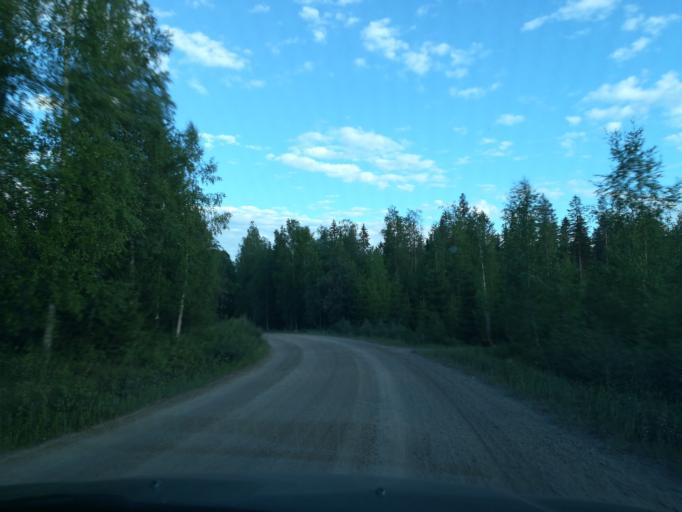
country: FI
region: Southern Savonia
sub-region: Mikkeli
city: Puumala
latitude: 61.6184
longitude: 28.1120
